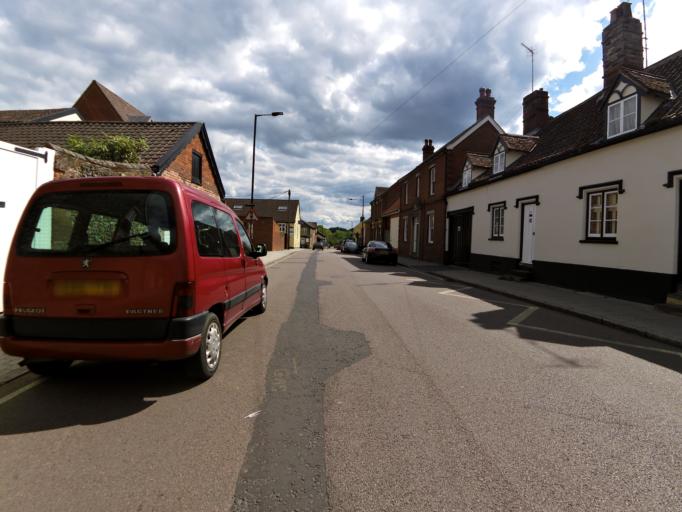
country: GB
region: England
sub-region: Suffolk
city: Bury St Edmunds
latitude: 52.2428
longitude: 0.7113
